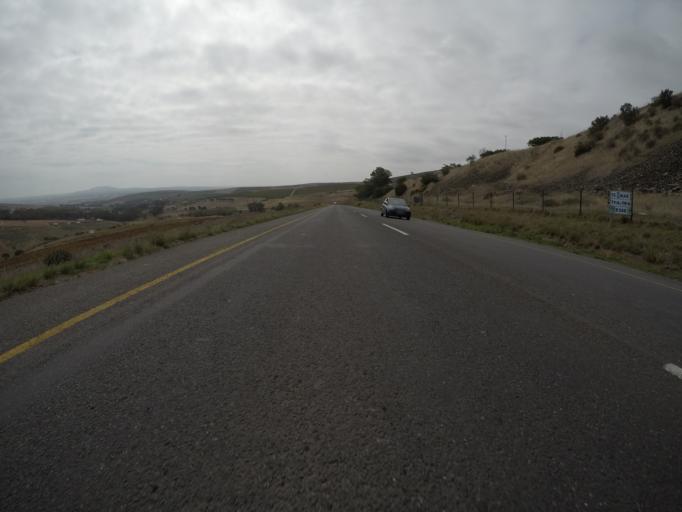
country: ZA
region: Western Cape
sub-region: City of Cape Town
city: Sunset Beach
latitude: -33.8308
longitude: 18.5893
